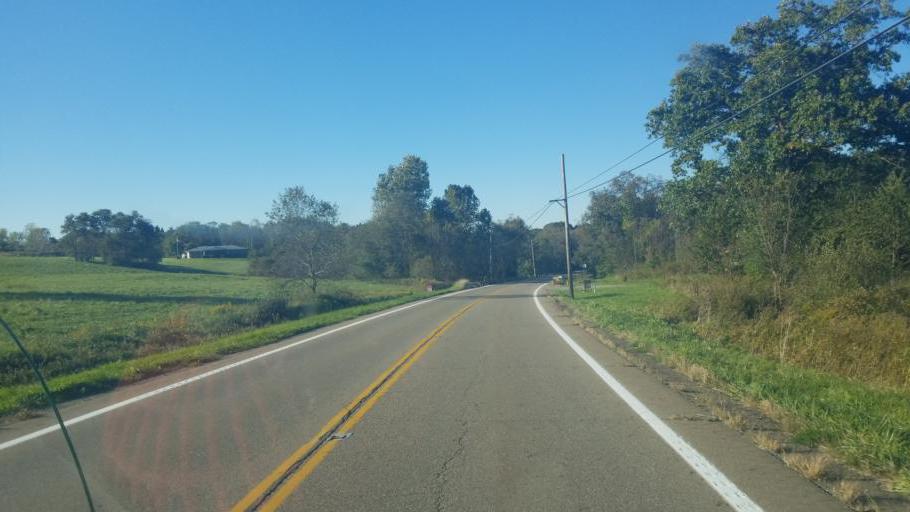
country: US
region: Ohio
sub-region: Columbiana County
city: Glenmoor
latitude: 40.6931
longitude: -80.6334
